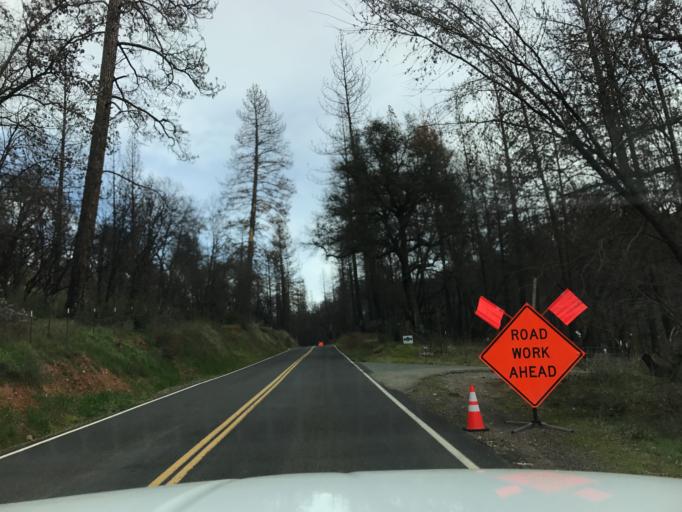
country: US
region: California
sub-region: Calaveras County
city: Mountain Ranch
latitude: 38.2345
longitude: -120.5278
